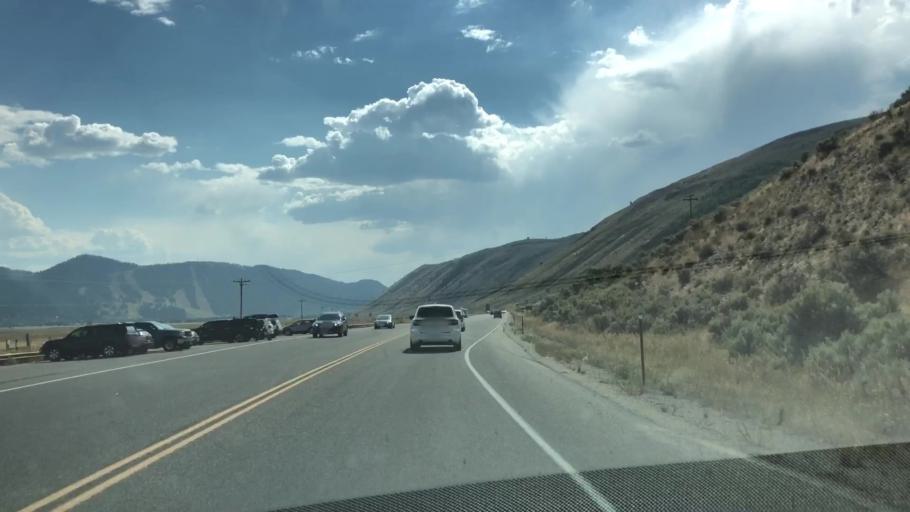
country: US
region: Wyoming
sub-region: Teton County
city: Jackson
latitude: 43.5206
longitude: -110.7439
